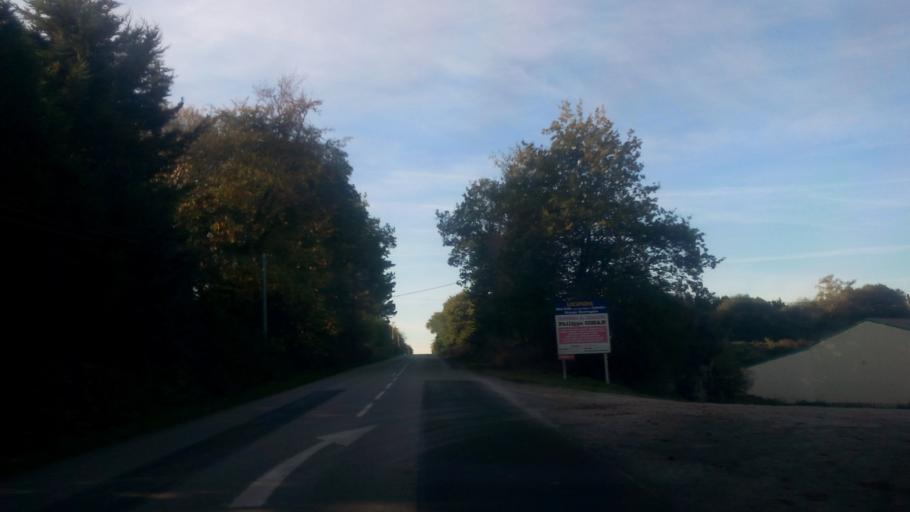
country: FR
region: Brittany
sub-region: Departement du Morbihan
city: La Vraie-Croix
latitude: 47.7072
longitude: -2.5560
